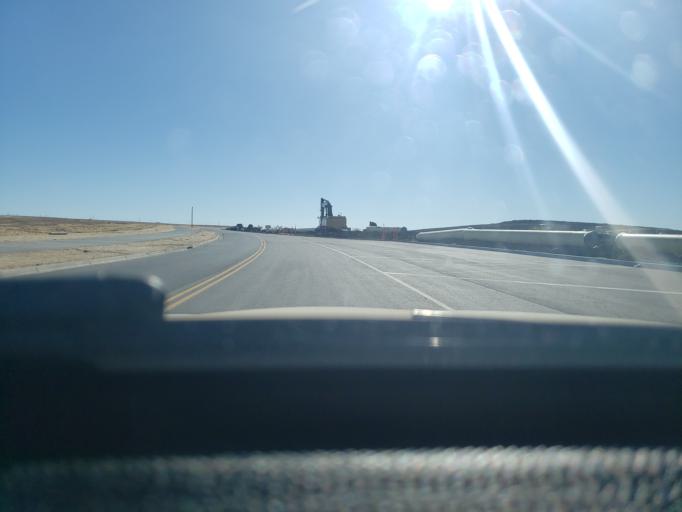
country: US
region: Colorado
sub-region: Adams County
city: Aurora
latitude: 39.7679
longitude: -104.7124
